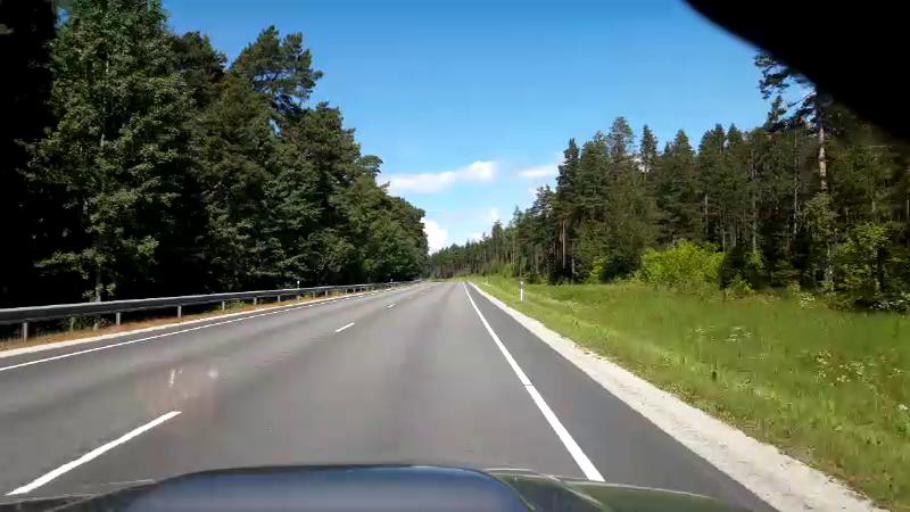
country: EE
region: Paernumaa
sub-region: Paernu linn
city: Parnu
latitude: 58.1573
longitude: 24.4984
